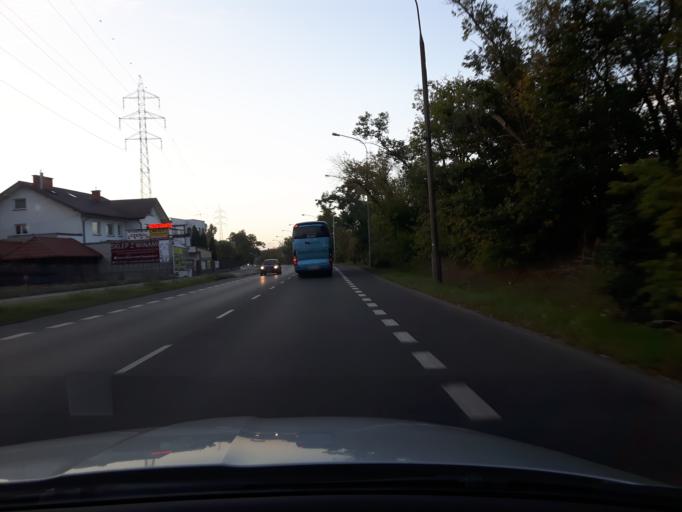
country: PL
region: Masovian Voivodeship
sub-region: Warszawa
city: Wawer
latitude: 52.2184
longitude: 21.1553
